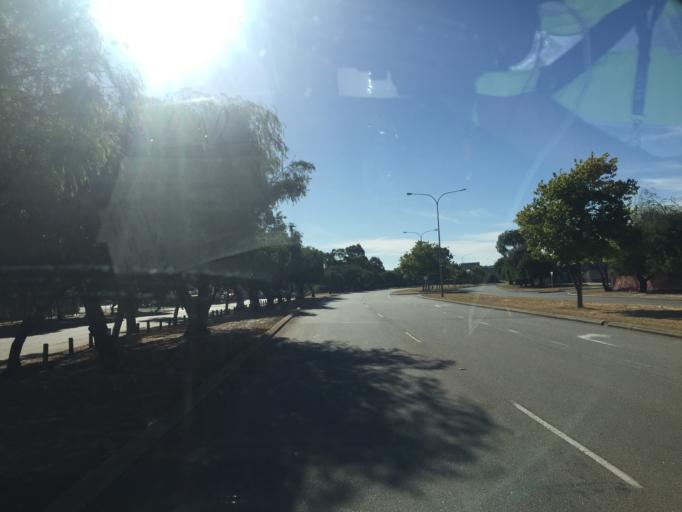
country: AU
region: Western Australia
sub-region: Canning
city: Queens Park
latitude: -31.9952
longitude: 115.9485
